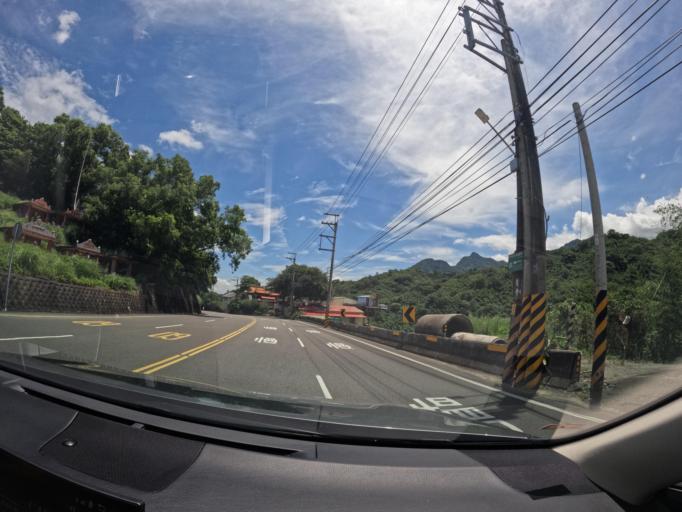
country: TW
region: Taiwan
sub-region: Miaoli
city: Miaoli
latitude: 24.5299
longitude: 120.9169
